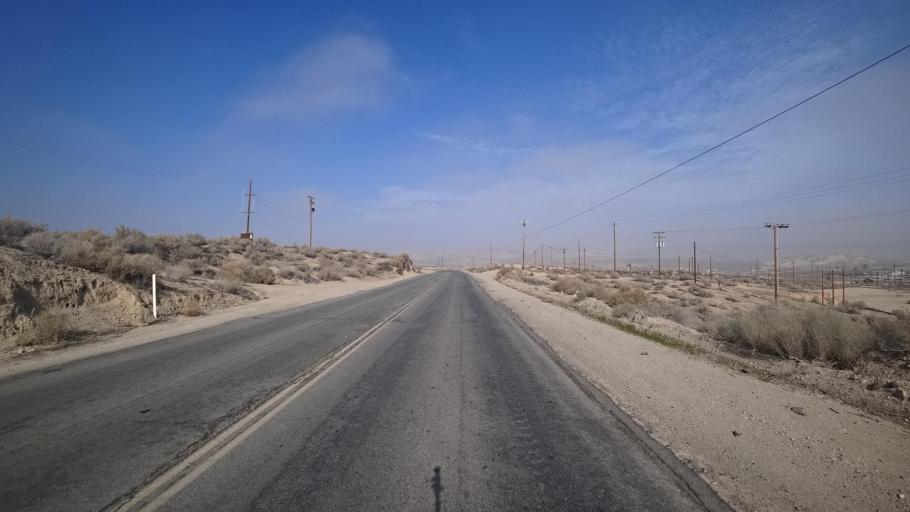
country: US
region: California
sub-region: Kern County
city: Ford City
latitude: 35.1790
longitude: -119.4654
